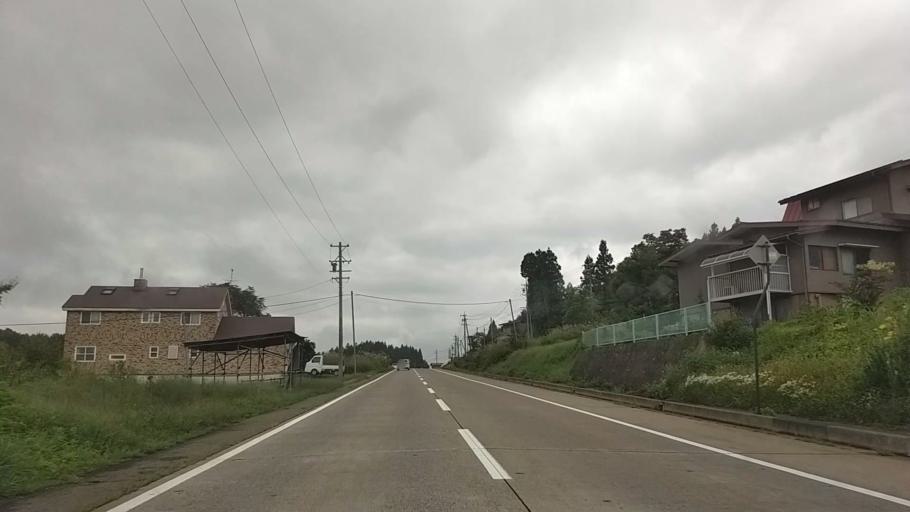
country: JP
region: Nagano
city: Iiyama
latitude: 36.8058
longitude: 138.3301
